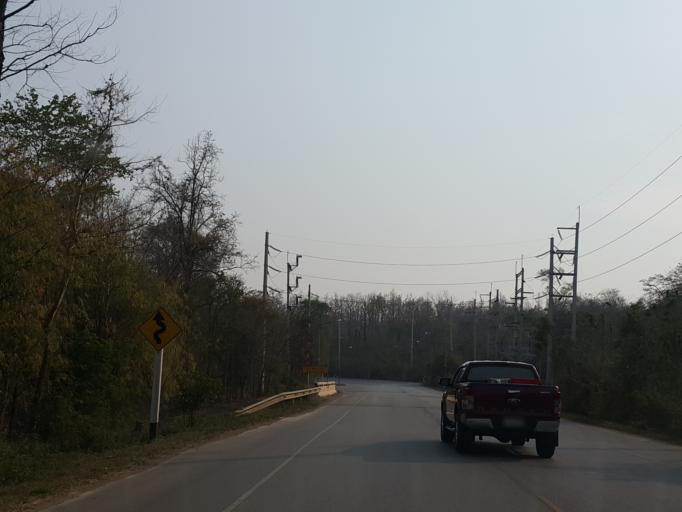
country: TH
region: Lampang
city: Chae Hom
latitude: 18.5457
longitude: 99.5678
